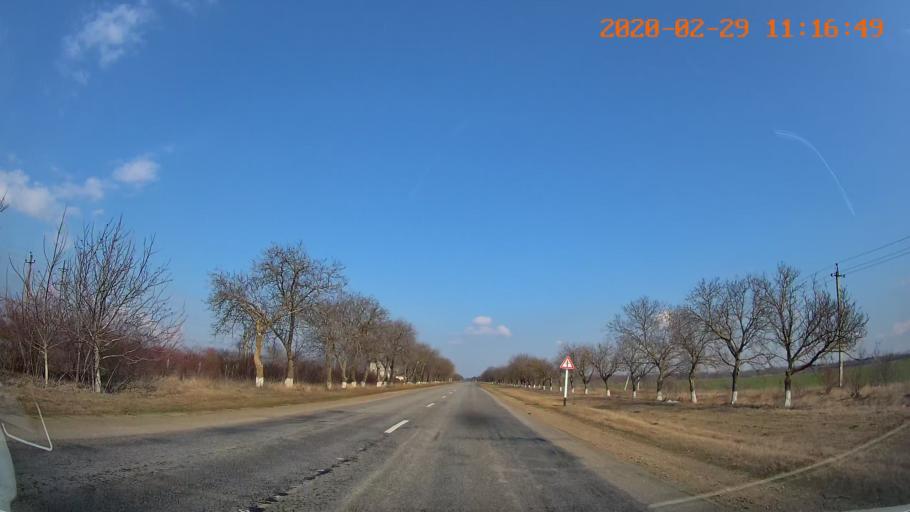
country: MD
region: Telenesti
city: Dubasari
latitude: 47.3138
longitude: 29.1688
